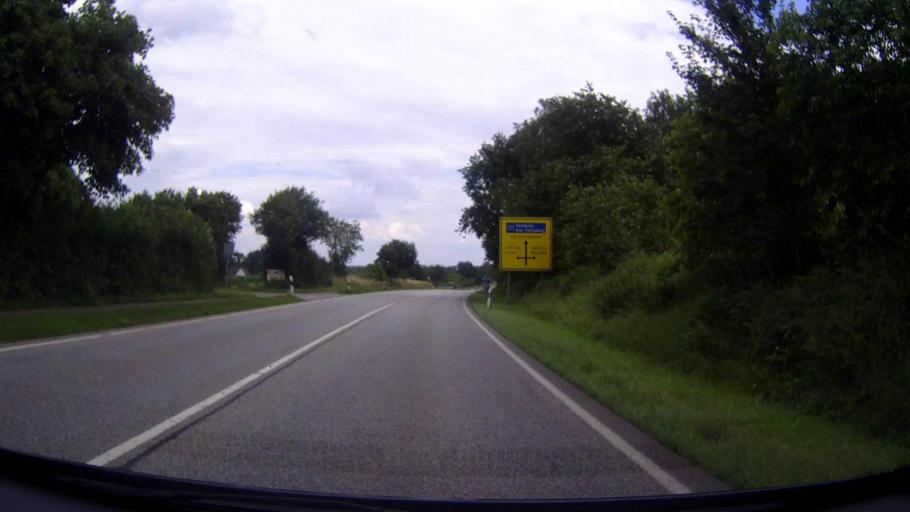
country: DE
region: Schleswig-Holstein
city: Aukrug
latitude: 54.0687
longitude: 9.7819
